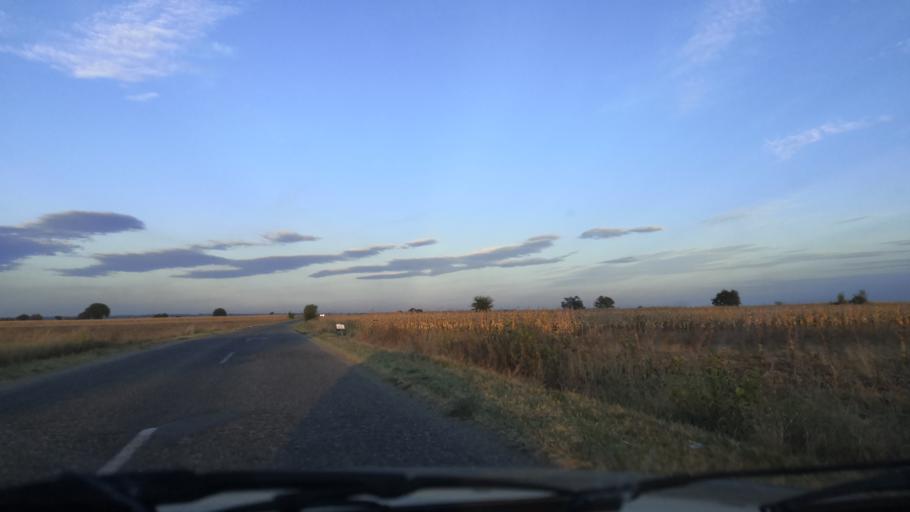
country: RO
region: Mehedinti
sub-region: Comuna Gruia
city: Izvoarele
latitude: 44.2535
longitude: 22.6217
